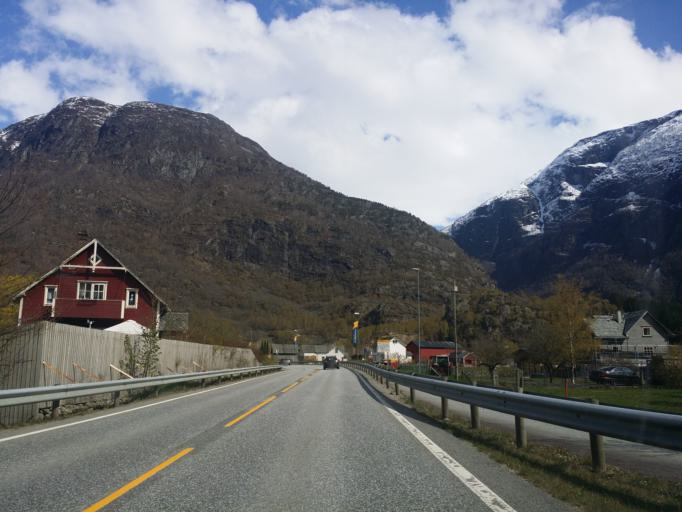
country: NO
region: Hordaland
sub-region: Eidfjord
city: Eidfjord
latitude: 60.4239
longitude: 7.1256
